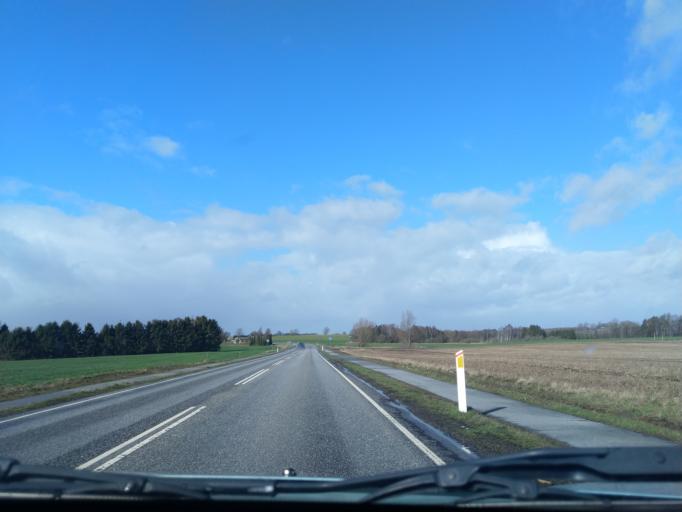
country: DK
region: Zealand
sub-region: Naestved Kommune
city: Naestved
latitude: 55.2897
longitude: 11.7045
